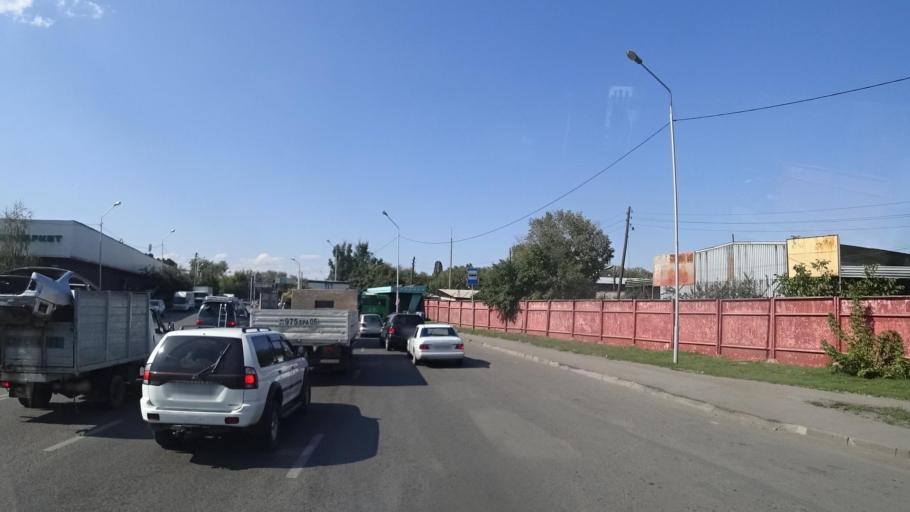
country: KZ
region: Almaty Oblysy
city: Pervomayskiy
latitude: 43.3459
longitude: 76.9708
